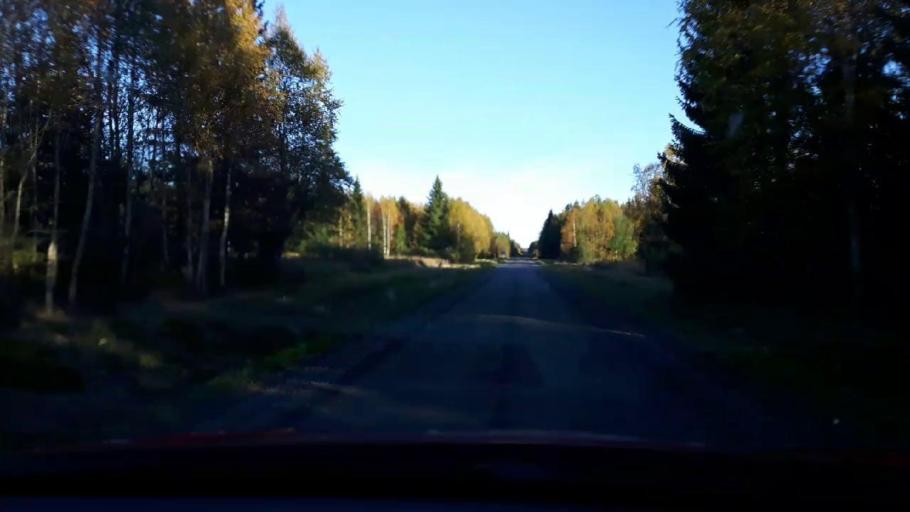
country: SE
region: Jaemtland
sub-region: OEstersunds Kommun
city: Lit
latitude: 63.6041
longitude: 14.7978
